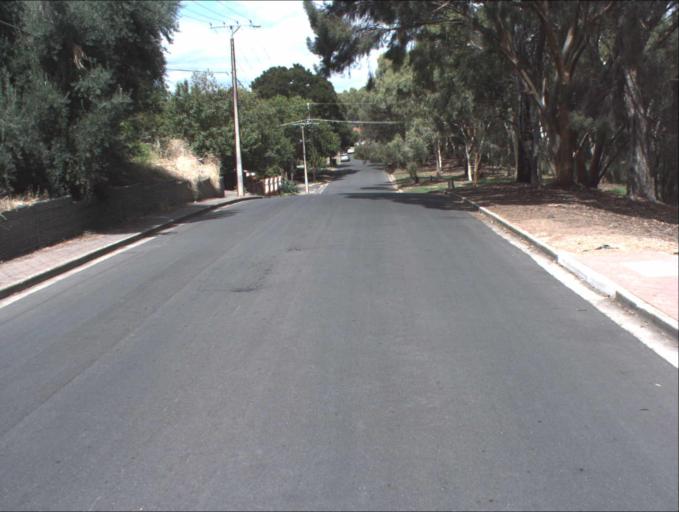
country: AU
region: South Australia
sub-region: Campbelltown
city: Paradise
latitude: -34.8636
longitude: 138.6671
